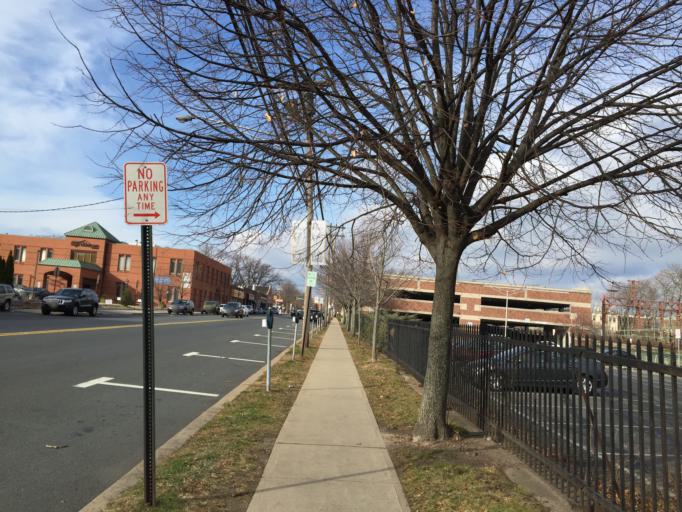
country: US
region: New Jersey
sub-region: Union County
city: Summit
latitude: 40.7151
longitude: -74.3539
